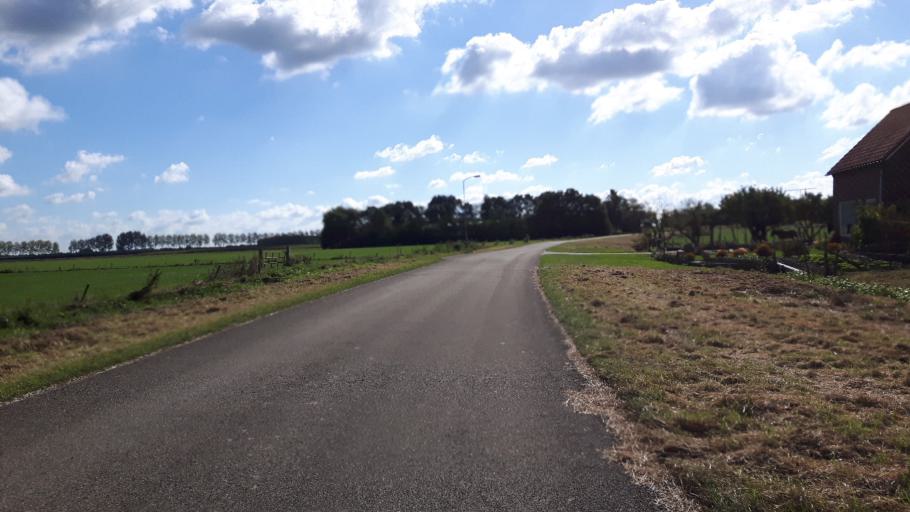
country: NL
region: Gelderland
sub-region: Gemeente Geldermalsen
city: Geldermalsen
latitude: 51.9307
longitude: 5.2846
